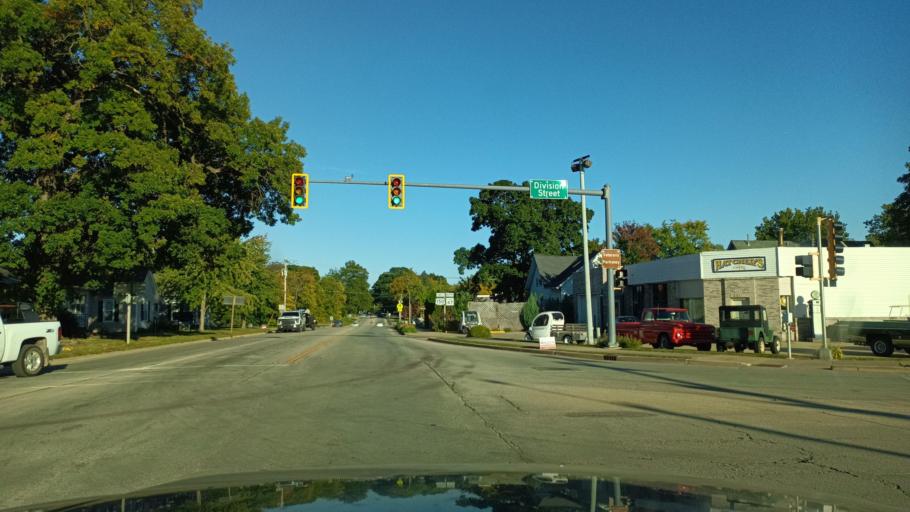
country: US
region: Illinois
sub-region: Champaign County
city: Mahomet
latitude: 40.1919
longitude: -88.4079
